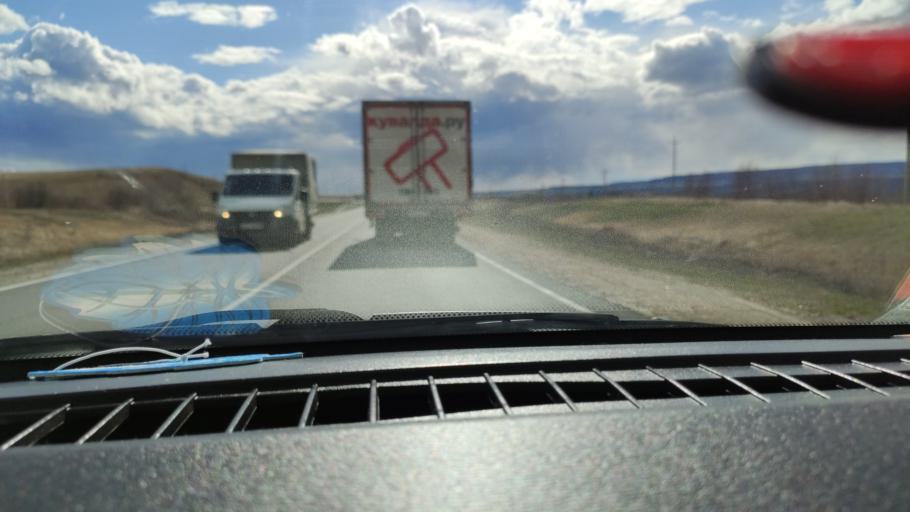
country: RU
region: Saratov
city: Alekseyevka
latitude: 52.3315
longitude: 47.9227
